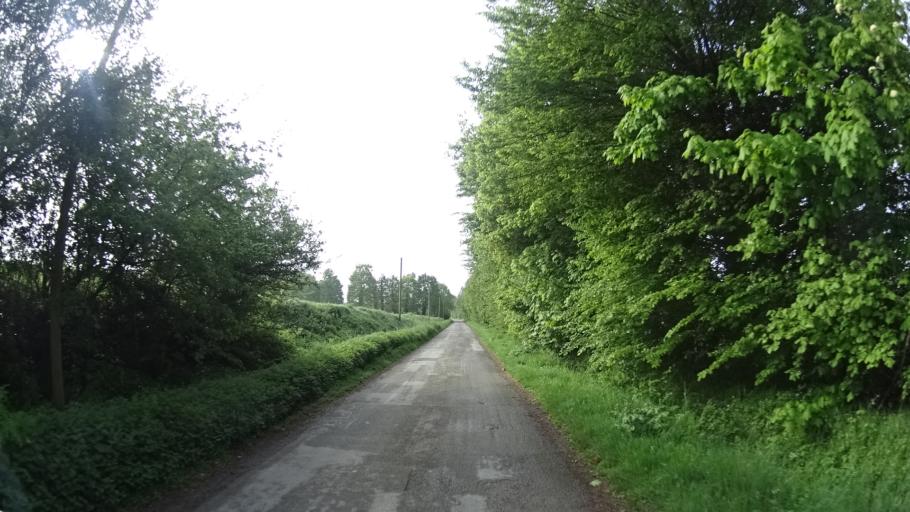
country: FR
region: Brittany
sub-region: Departement d'Ille-et-Vilaine
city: Mordelles
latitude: 48.0896
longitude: -1.8560
